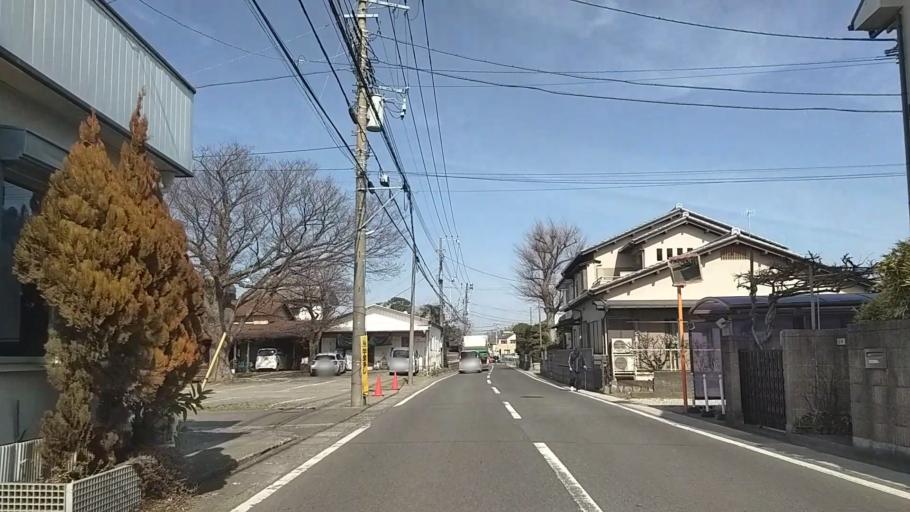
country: JP
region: Kanagawa
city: Chigasaki
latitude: 35.3807
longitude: 139.3835
